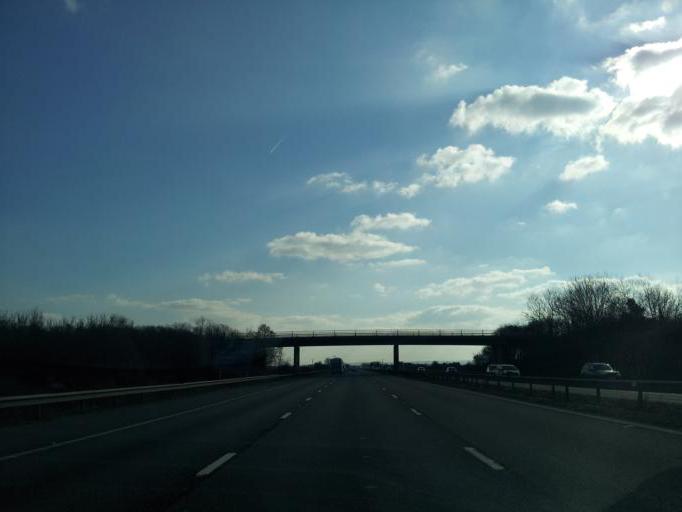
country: GB
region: England
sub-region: Somerset
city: Highbridge
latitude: 51.2330
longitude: -2.9486
